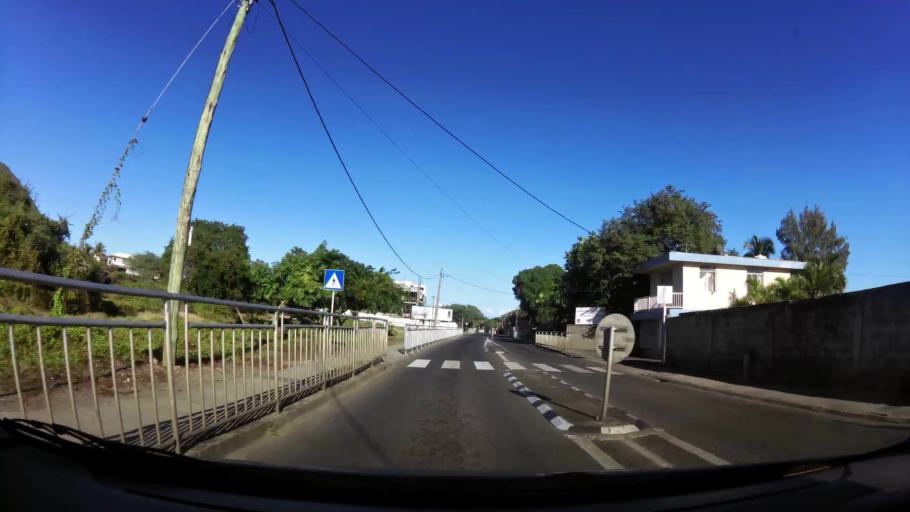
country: MU
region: Black River
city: Tamarin
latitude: -20.3297
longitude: 57.3740
